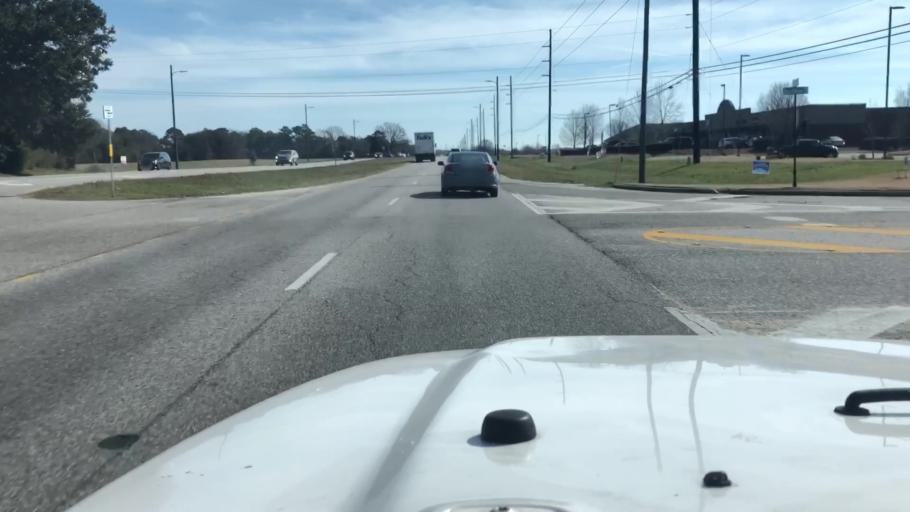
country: US
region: Alabama
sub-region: Montgomery County
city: Pike Road
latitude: 32.3793
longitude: -86.1572
